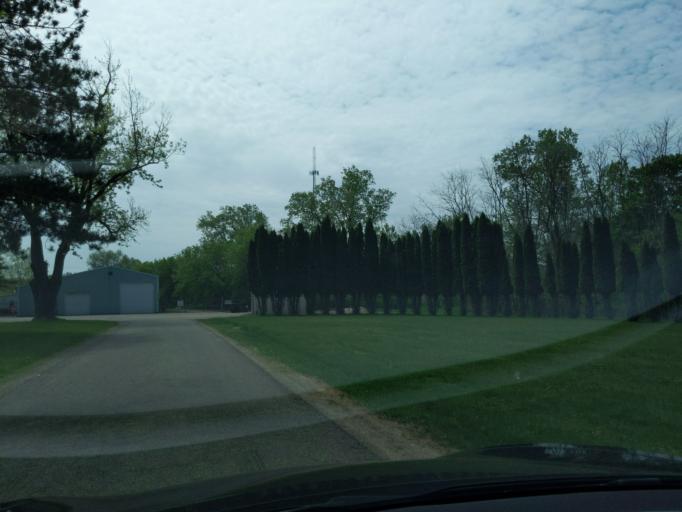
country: US
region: Michigan
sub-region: Ingham County
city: Stockbridge
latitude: 42.4473
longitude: -84.1753
